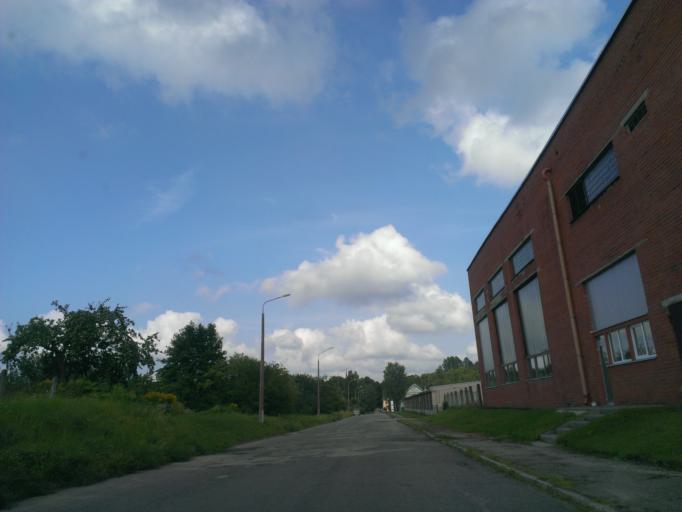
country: LV
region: Priekuli
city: Priekuli
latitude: 57.3081
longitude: 25.3636
